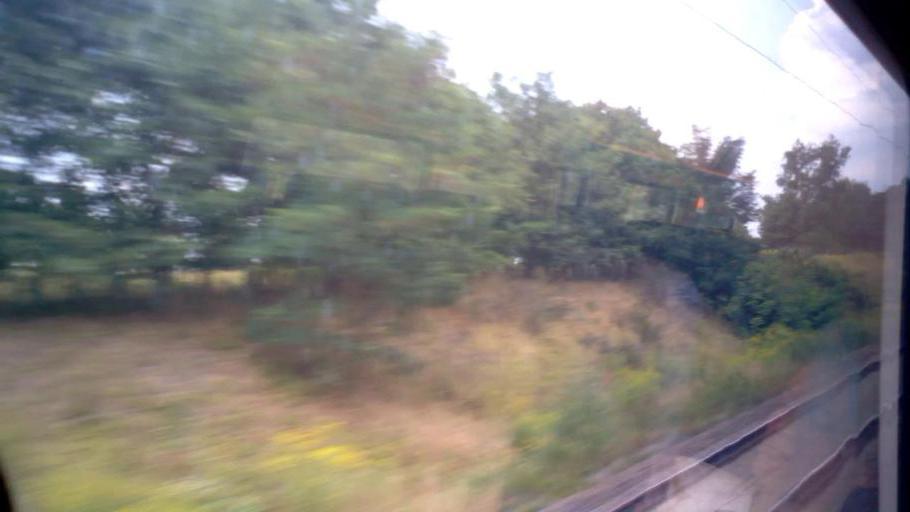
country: DE
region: Brandenburg
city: Grossbeeren
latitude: 52.3737
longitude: 13.2940
